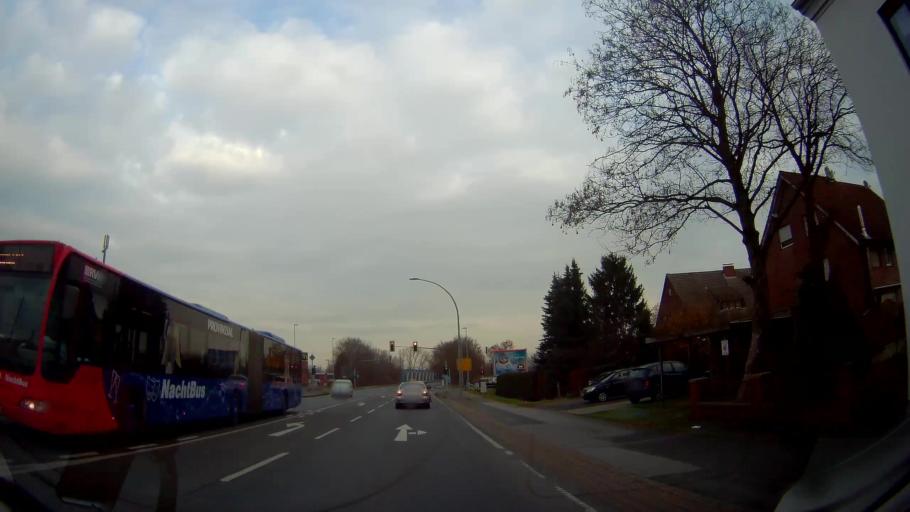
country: DE
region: North Rhine-Westphalia
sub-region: Regierungsbezirk Munster
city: Haltern
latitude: 51.7267
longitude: 7.1868
